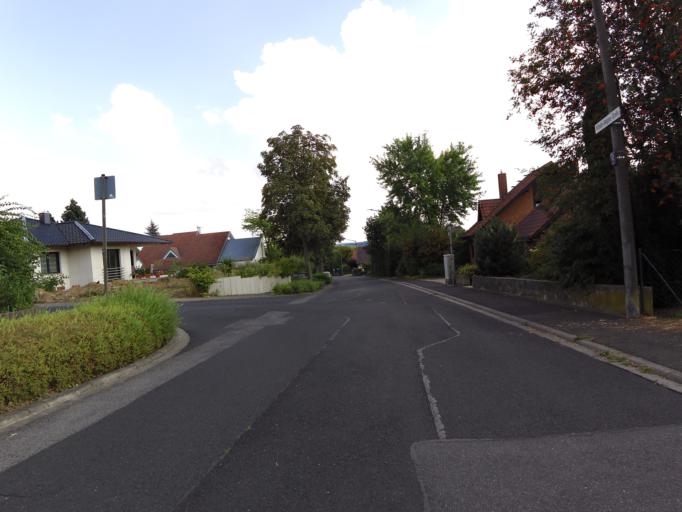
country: DE
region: Bavaria
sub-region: Regierungsbezirk Unterfranken
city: Estenfeld
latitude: 49.8257
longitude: 9.9979
